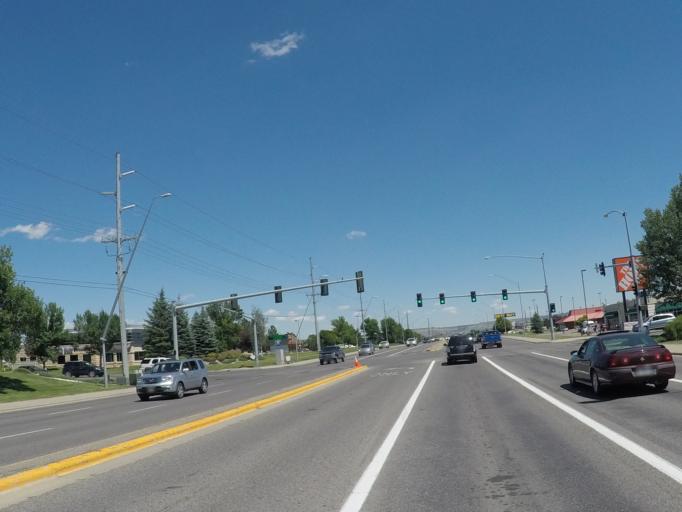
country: US
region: Montana
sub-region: Yellowstone County
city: Billings
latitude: 45.7552
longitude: -108.5820
